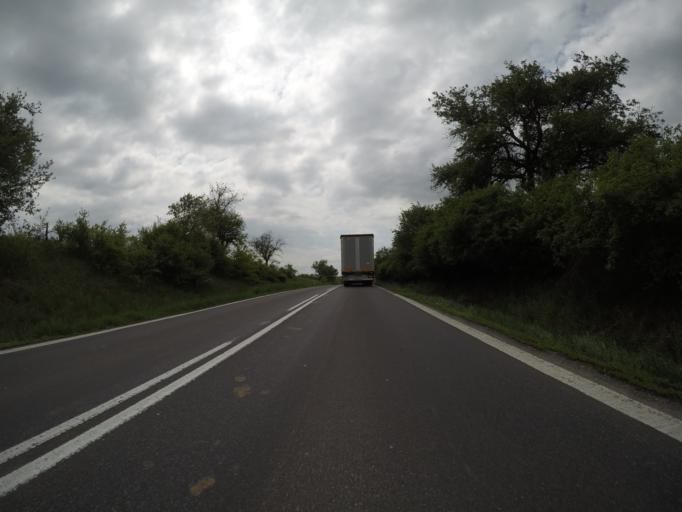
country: SK
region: Banskobystricky
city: Krupina
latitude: 48.2993
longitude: 19.0231
